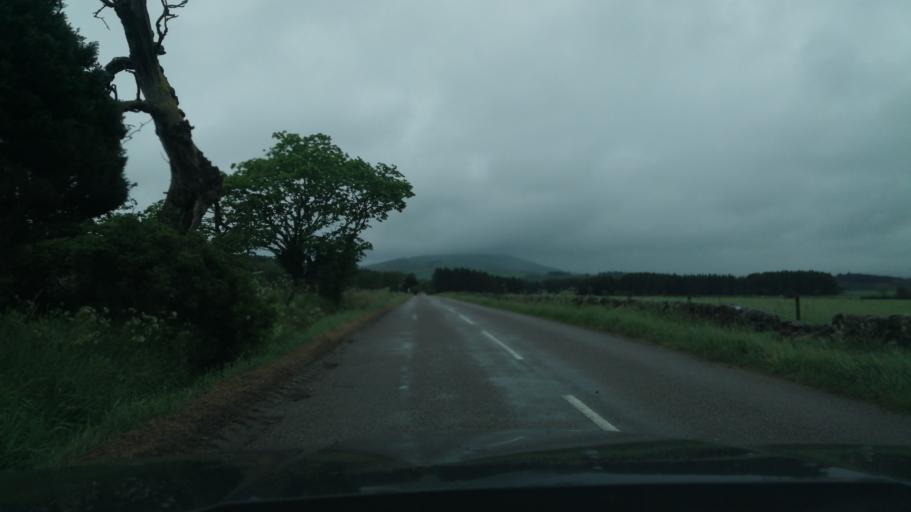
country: GB
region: Scotland
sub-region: Aberdeenshire
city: Huntly
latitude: 57.5364
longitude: -2.7728
